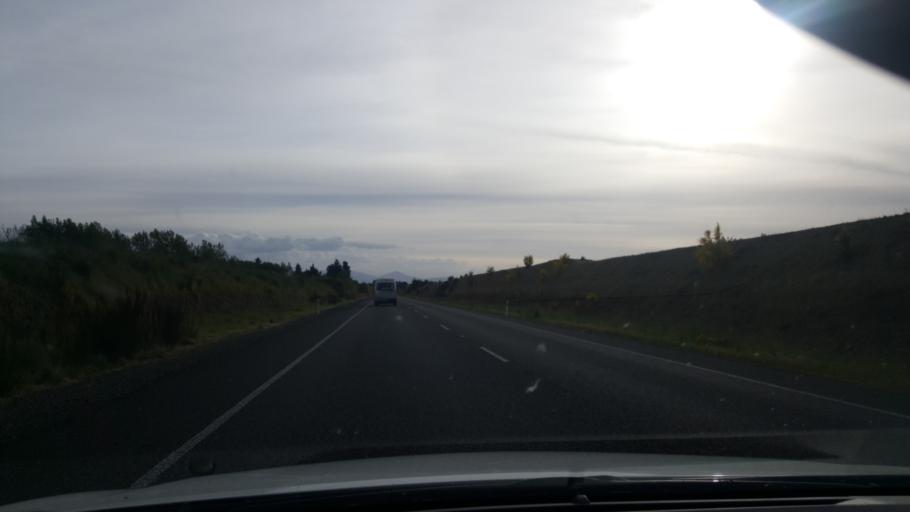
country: NZ
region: Waikato
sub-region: Taupo District
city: Taupo
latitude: -38.7274
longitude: 176.0905
